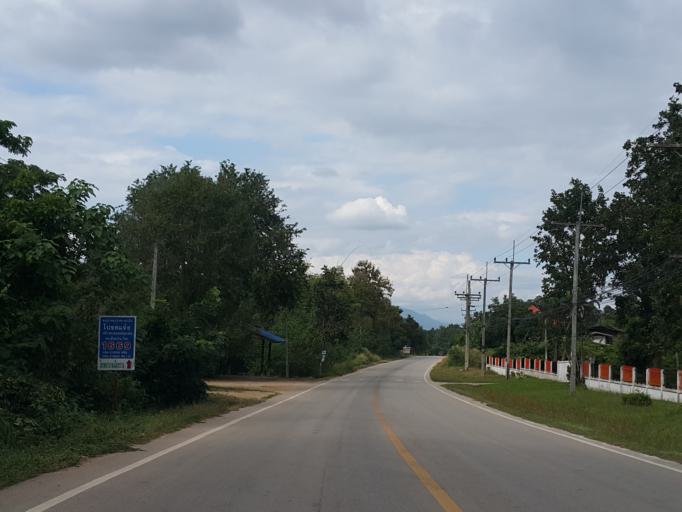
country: TH
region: Lampang
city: Chae Hom
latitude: 18.5633
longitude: 99.4730
